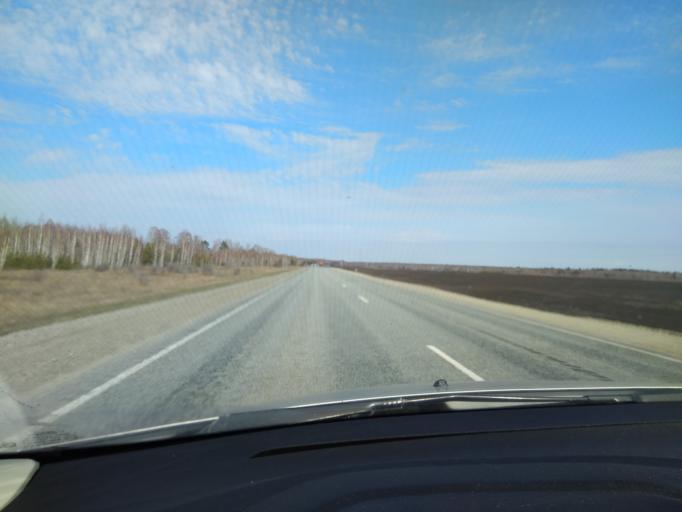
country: RU
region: Sverdlovsk
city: Tugulym
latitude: 57.0735
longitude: 64.7071
